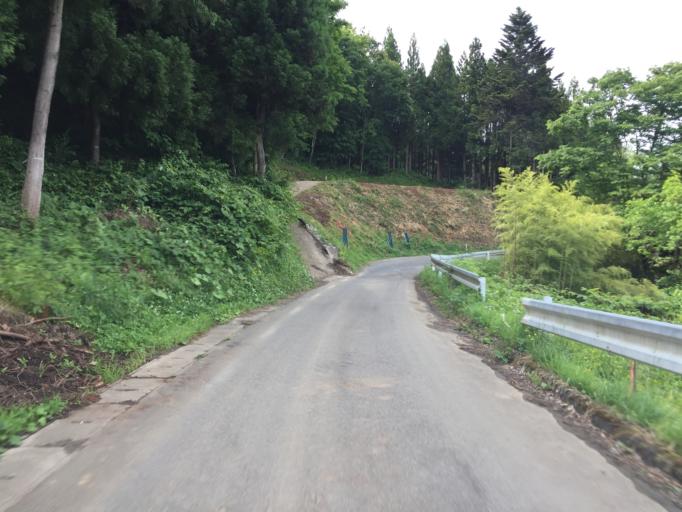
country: JP
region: Fukushima
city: Funehikimachi-funehiki
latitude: 37.5109
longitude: 140.6498
